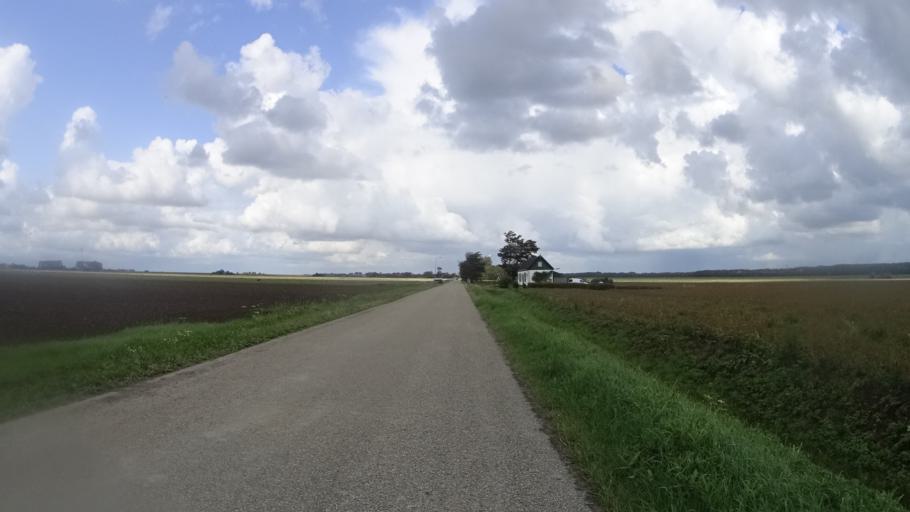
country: NL
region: North Holland
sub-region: Gemeente Schagen
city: Schagen
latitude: 52.8532
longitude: 4.8848
